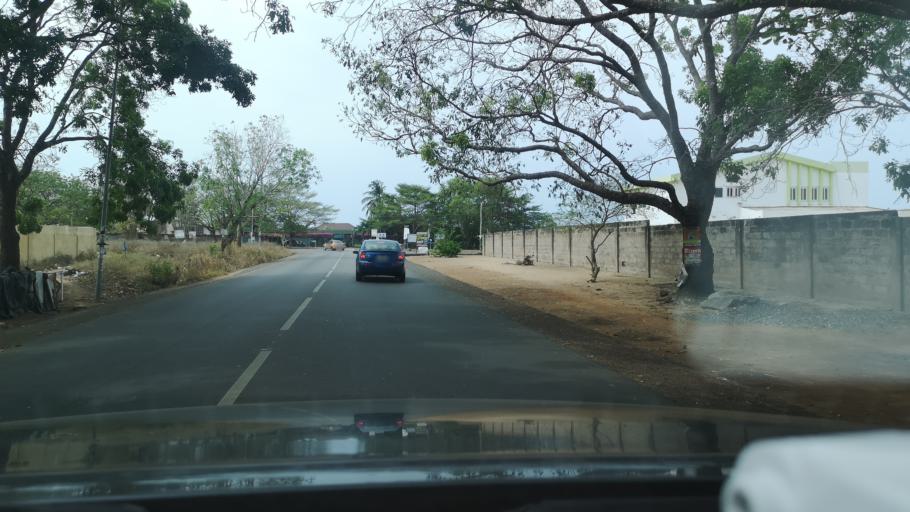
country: GH
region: Greater Accra
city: Tema
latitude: 5.6614
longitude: -0.0260
